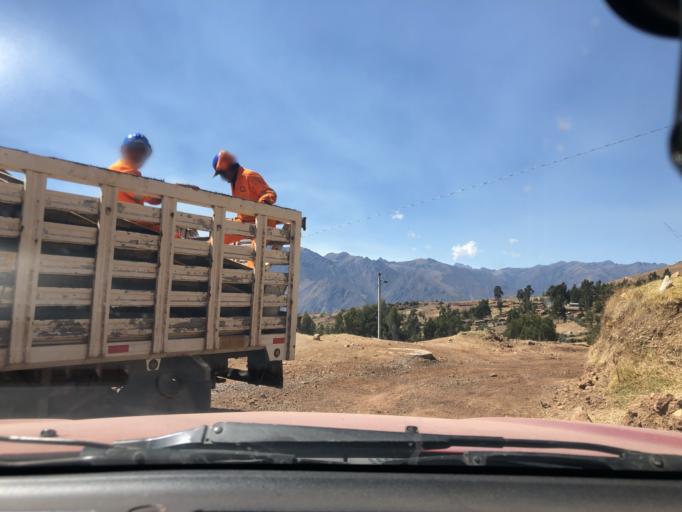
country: PE
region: Ayacucho
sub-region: Provincia de La Mar
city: Chilcas
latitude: -13.1686
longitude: -73.8552
